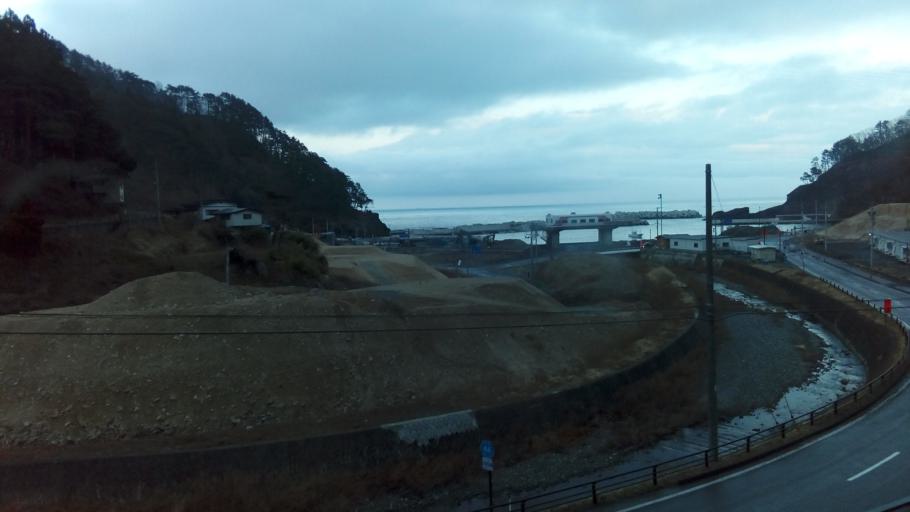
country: JP
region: Iwate
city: Miyako
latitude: 39.9169
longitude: 141.9397
